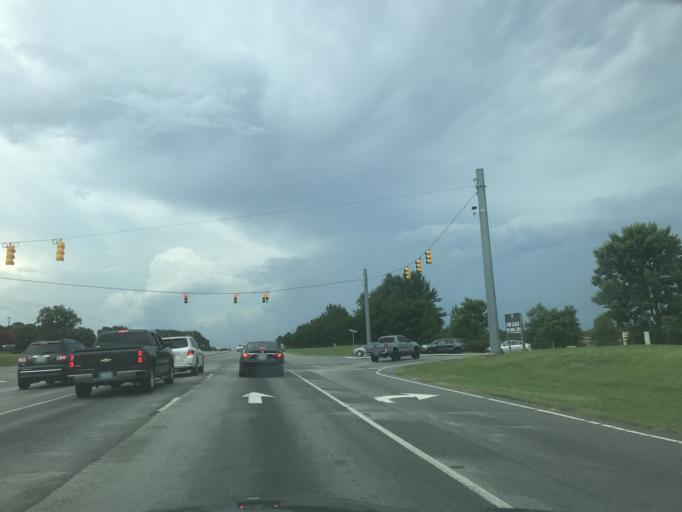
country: US
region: North Carolina
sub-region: Johnston County
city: Clayton
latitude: 35.6653
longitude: -78.4972
